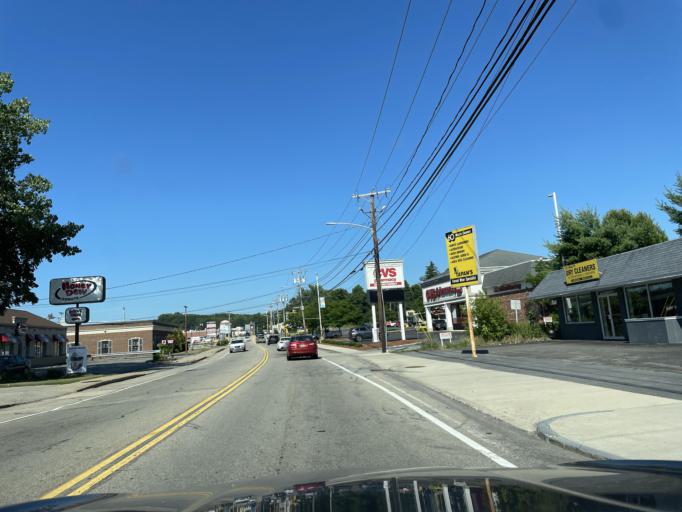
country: US
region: Massachusetts
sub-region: Worcester County
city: Webster
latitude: 42.0585
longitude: -71.8673
